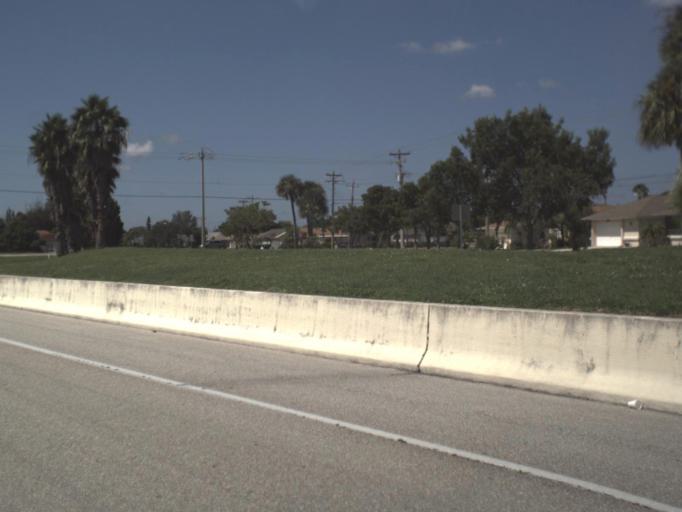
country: US
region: Florida
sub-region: Lee County
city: Cape Coral
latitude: 26.6063
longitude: -81.9549
